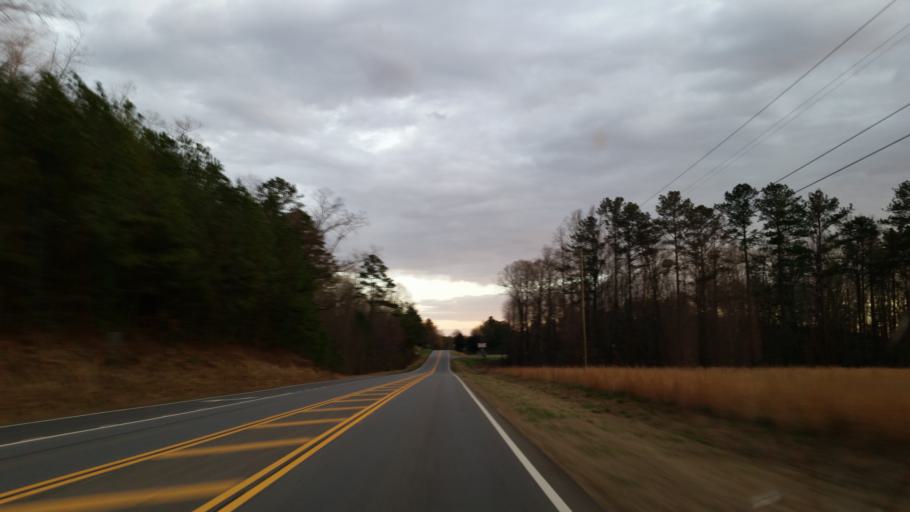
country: US
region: Georgia
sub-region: Pickens County
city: Jasper
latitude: 34.4411
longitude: -84.3993
